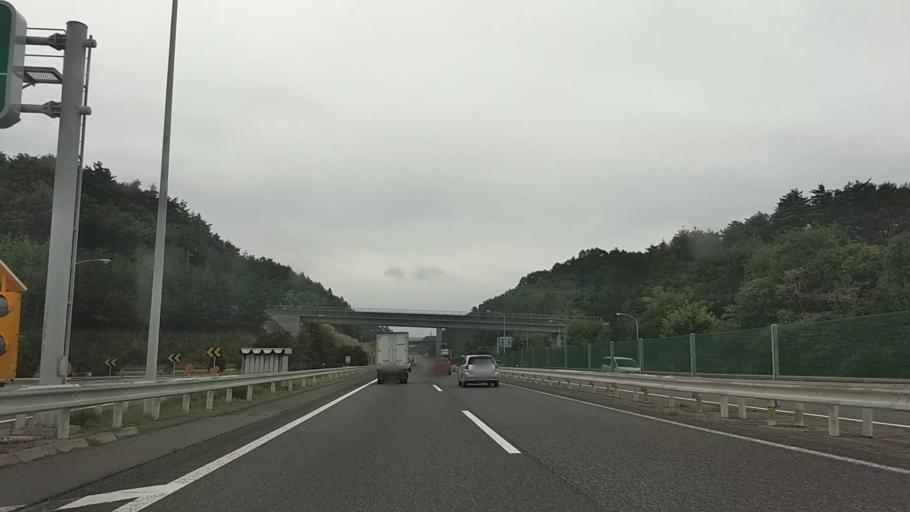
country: JP
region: Nagano
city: Shiojiri
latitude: 36.1184
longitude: 137.9817
